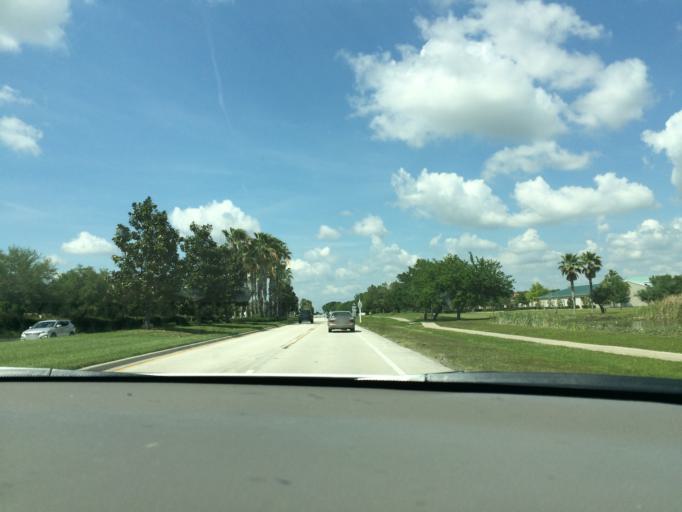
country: US
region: Florida
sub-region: Sarasota County
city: The Meadows
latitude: 27.3891
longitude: -82.3981
